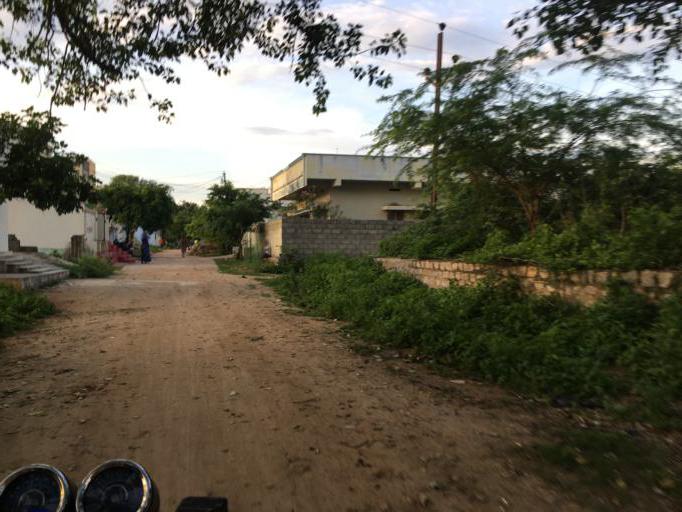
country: IN
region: Telangana
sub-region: Nalgonda
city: Nalgonda
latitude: 17.1731
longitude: 79.4177
